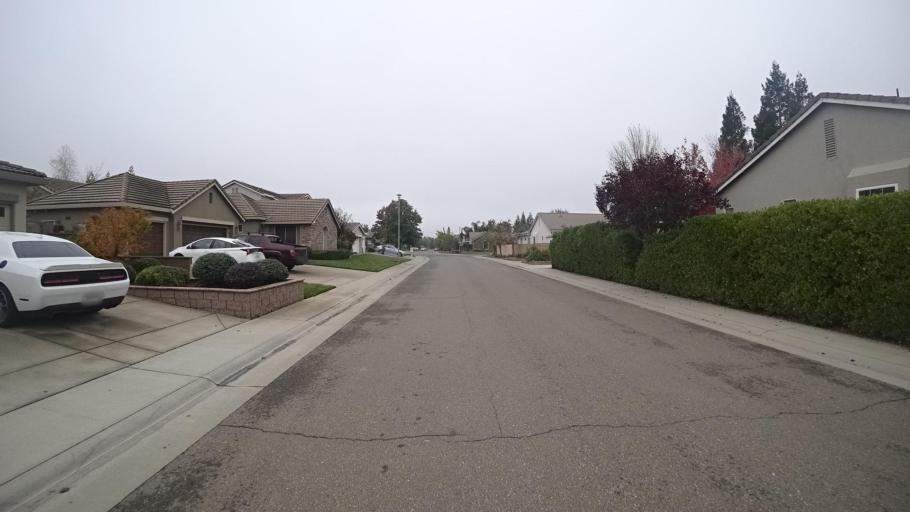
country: US
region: California
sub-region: Sacramento County
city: Elk Grove
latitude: 38.4080
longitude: -121.3374
